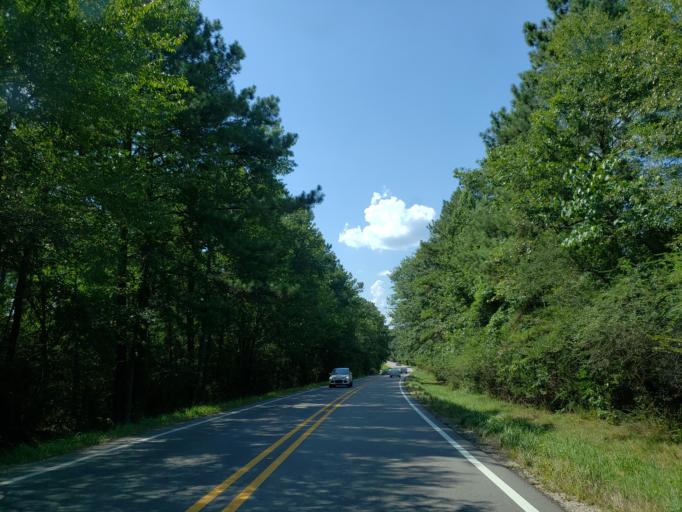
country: US
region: Mississippi
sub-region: Lamar County
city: Sumrall
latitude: 31.3822
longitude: -89.5261
